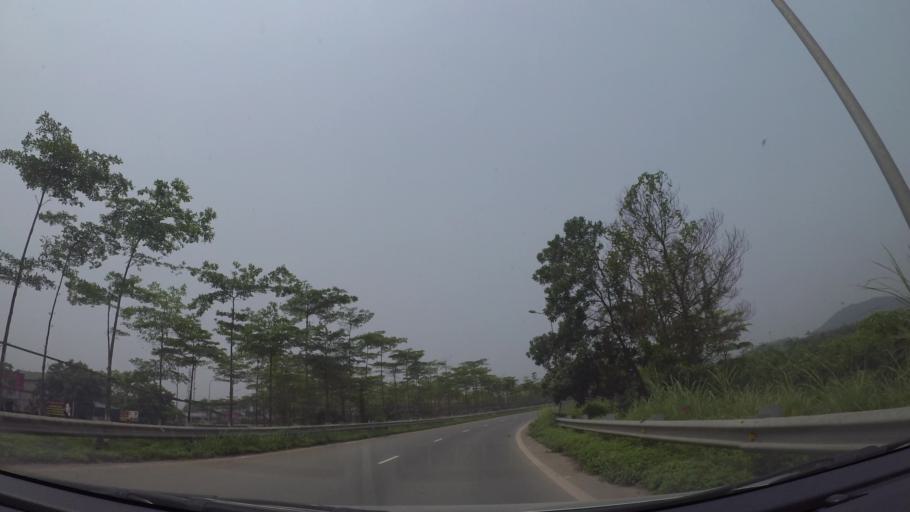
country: VN
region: Ha Noi
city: Lien Quan
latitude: 20.9877
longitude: 105.5271
